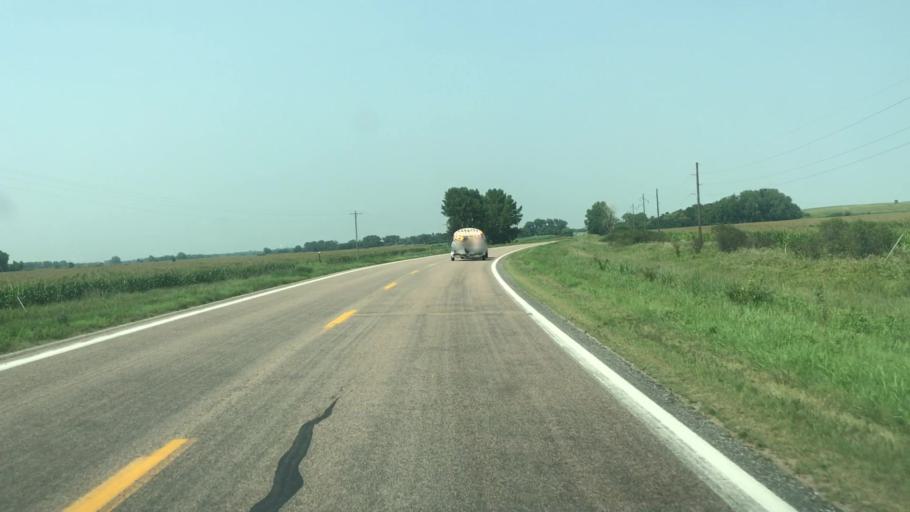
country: US
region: Nebraska
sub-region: Sherman County
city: Loup City
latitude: 41.2362
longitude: -98.9384
